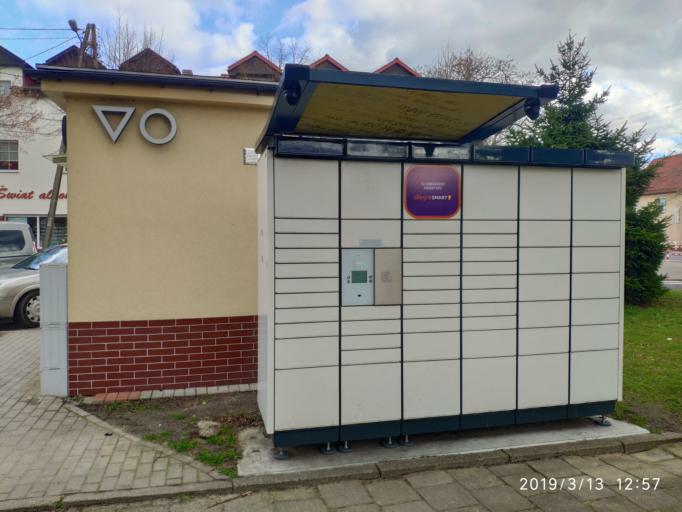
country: PL
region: Lubusz
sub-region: Powiat zielonogorski
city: Nowogrod Bobrzanski
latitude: 51.7988
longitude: 15.2350
